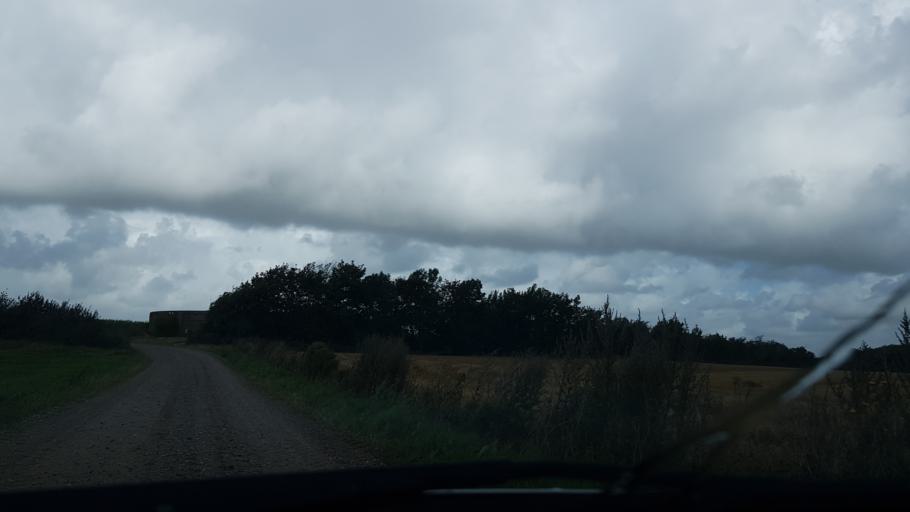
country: DK
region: South Denmark
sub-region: Esbjerg Kommune
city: Ribe
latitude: 55.2440
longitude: 8.7830
